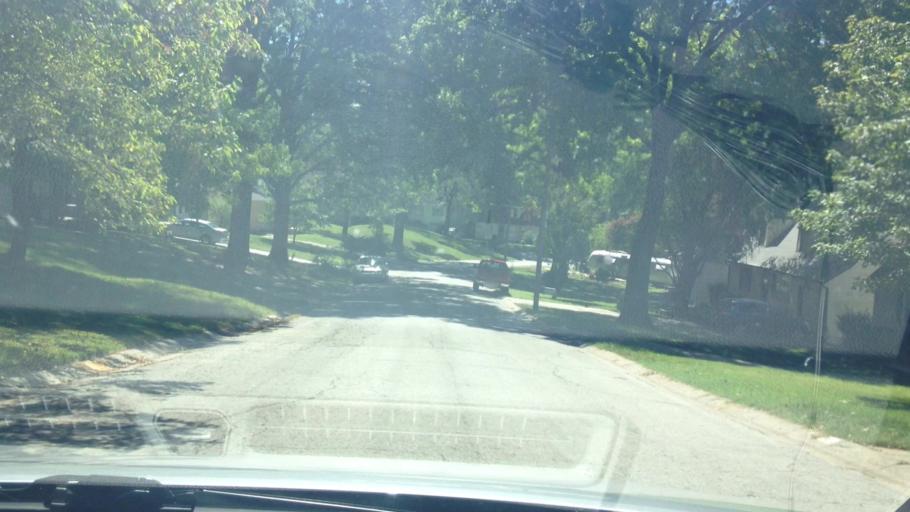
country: US
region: Kansas
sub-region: Johnson County
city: Leawood
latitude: 38.9661
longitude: -94.6022
